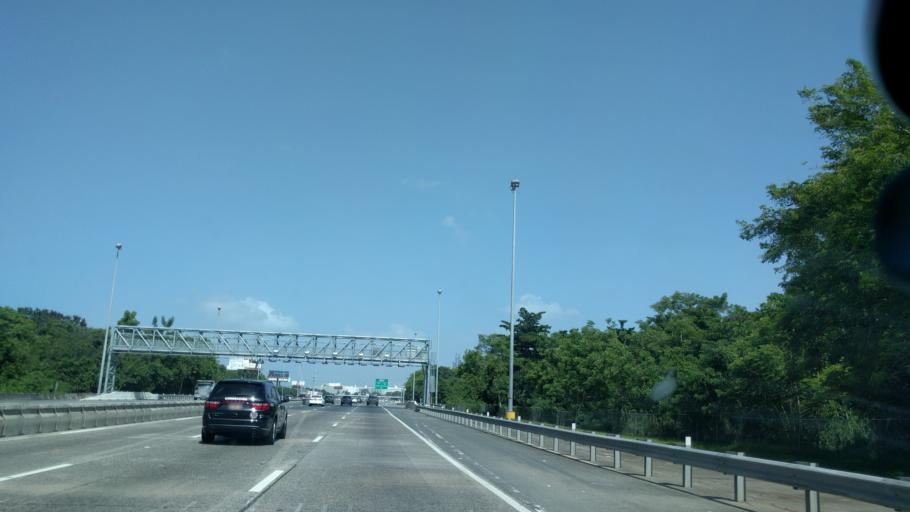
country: PR
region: Catano
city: Catano
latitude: 18.4226
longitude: -66.1281
